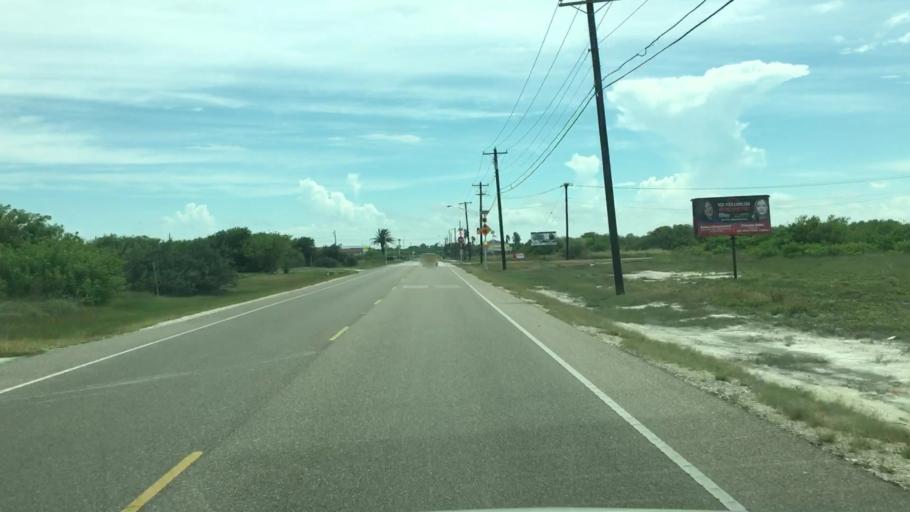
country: US
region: Texas
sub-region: Nueces County
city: Corpus Christi
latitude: 27.6447
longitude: -97.2840
